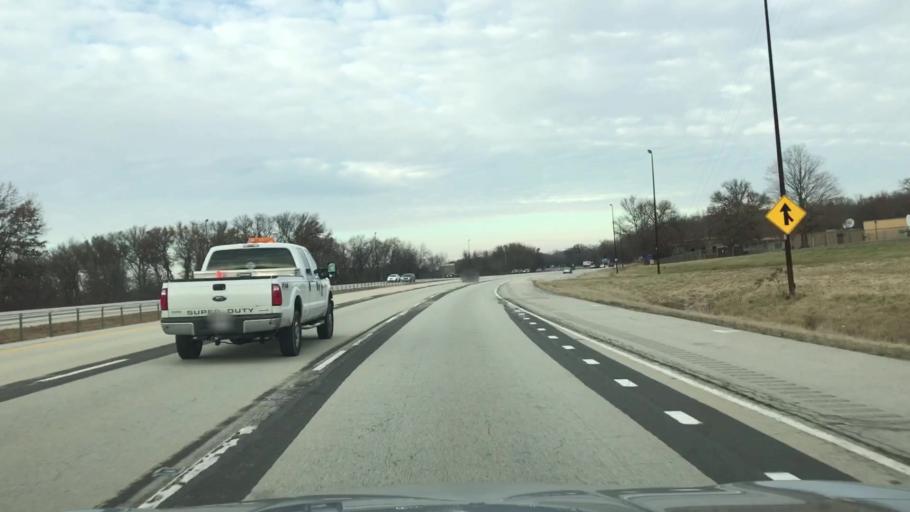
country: US
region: Illinois
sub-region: Sangamon County
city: Chatham
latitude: 39.6881
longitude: -89.6433
